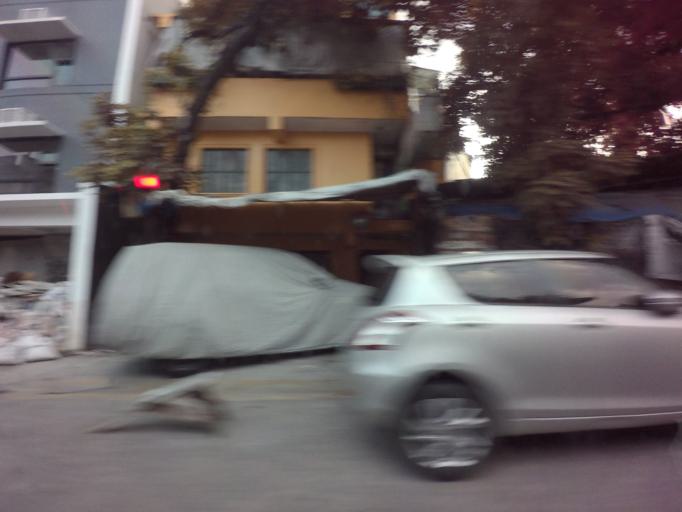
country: PH
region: Metro Manila
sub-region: Makati City
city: Makati City
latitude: 14.5629
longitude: 121.0499
